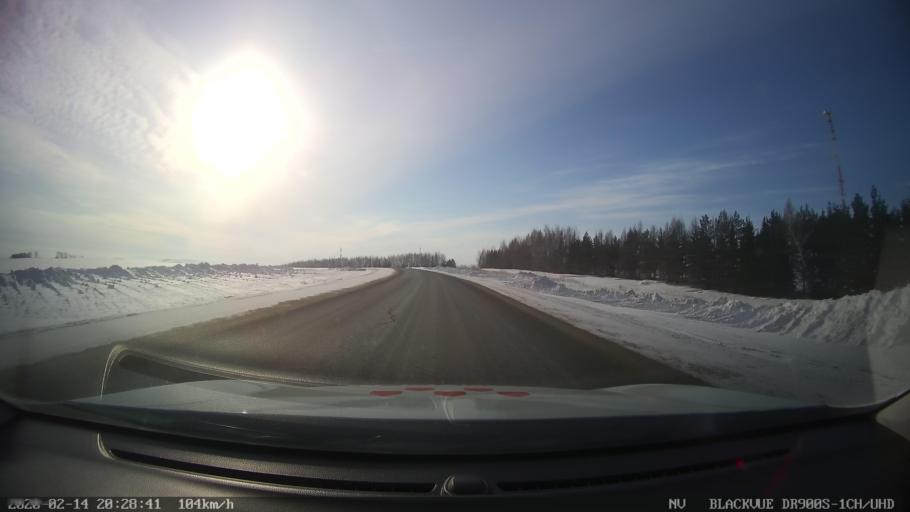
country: RU
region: Tatarstan
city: Stolbishchi
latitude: 55.4596
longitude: 48.9774
